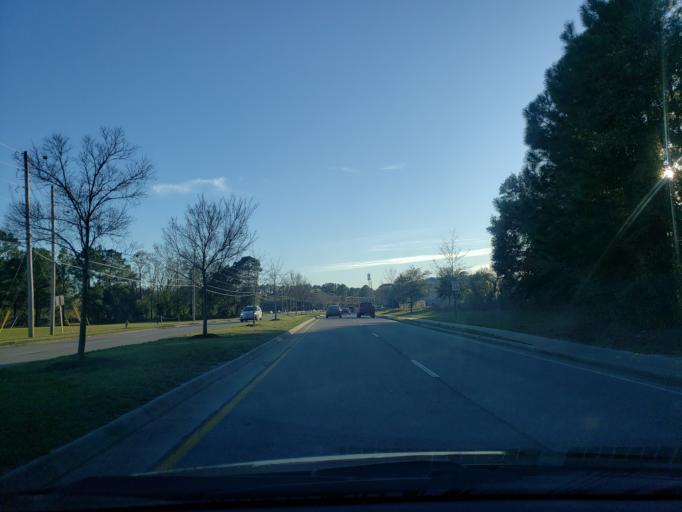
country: US
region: Georgia
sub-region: Chatham County
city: Montgomery
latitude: 32.0000
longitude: -81.1456
